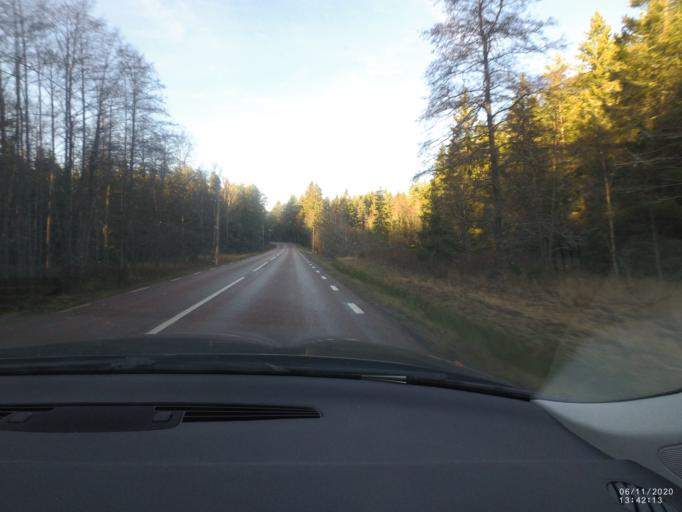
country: SE
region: Soedermanland
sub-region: Nykopings Kommun
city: Nykoping
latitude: 58.8458
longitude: 17.0638
